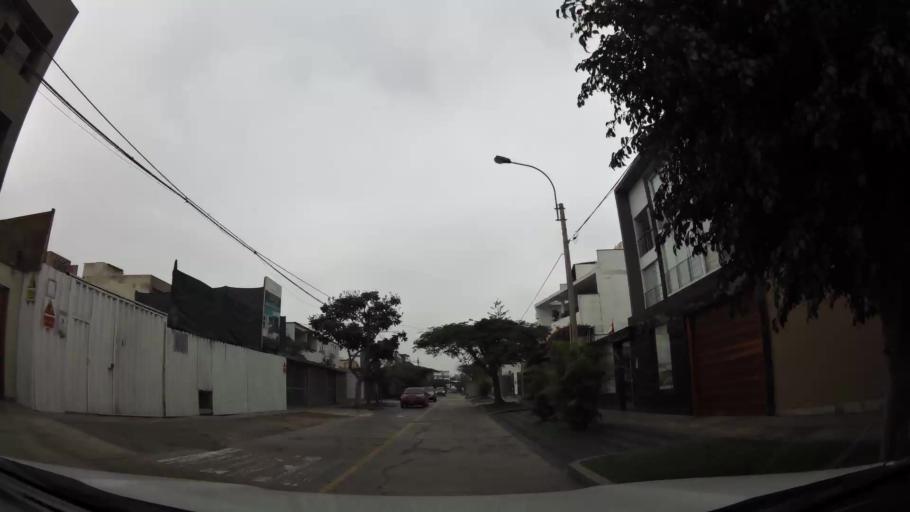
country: PE
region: Lima
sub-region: Lima
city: San Luis
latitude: -12.1045
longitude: -76.9824
